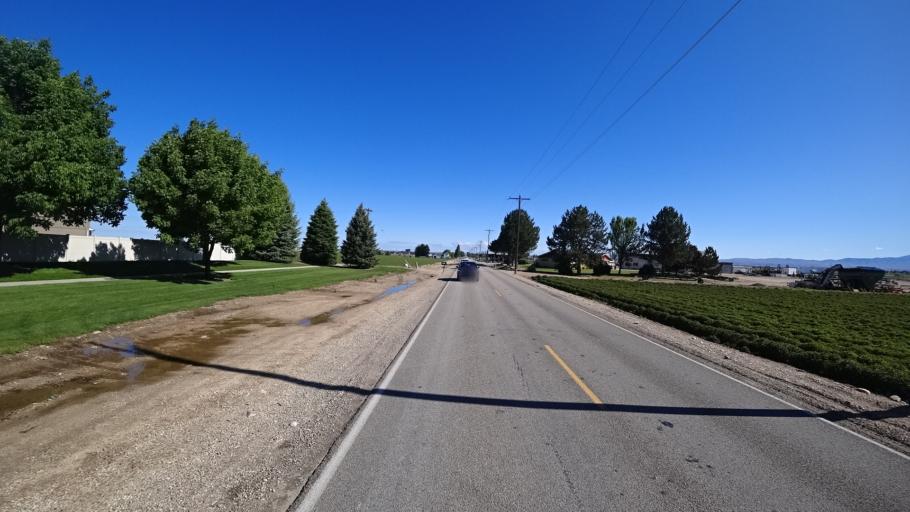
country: US
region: Idaho
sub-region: Ada County
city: Meridian
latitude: 43.6373
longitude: -116.4536
